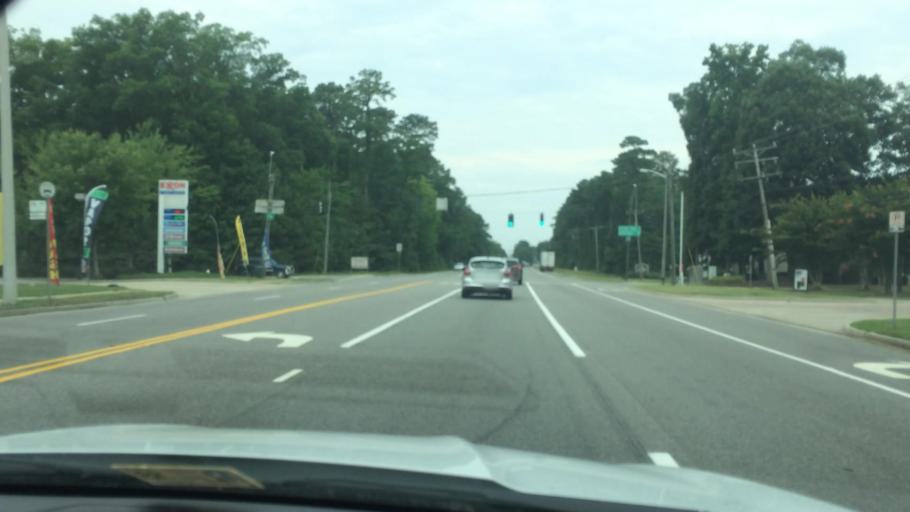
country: US
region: Virginia
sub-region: York County
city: Yorktown
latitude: 37.1714
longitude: -76.5457
